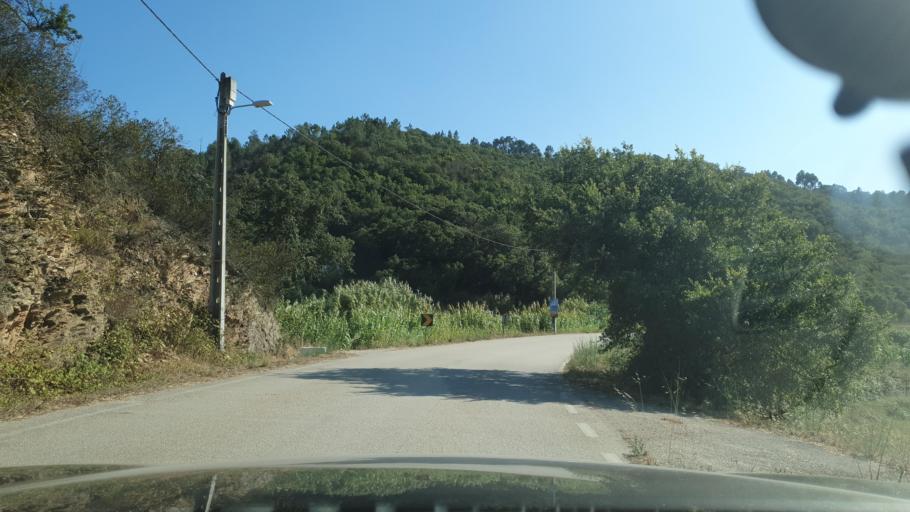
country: PT
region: Beja
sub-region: Odemira
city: Sao Teotonio
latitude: 37.4318
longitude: -8.7745
